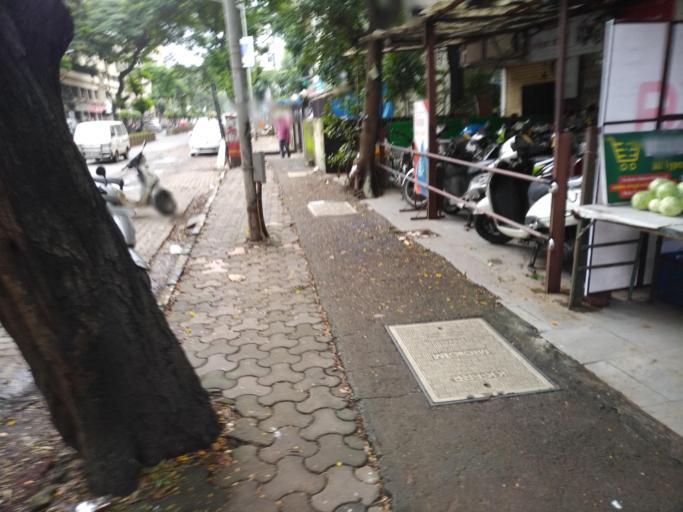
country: IN
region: Maharashtra
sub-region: Mumbai Suburban
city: Borivli
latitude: 19.2417
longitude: 72.8650
